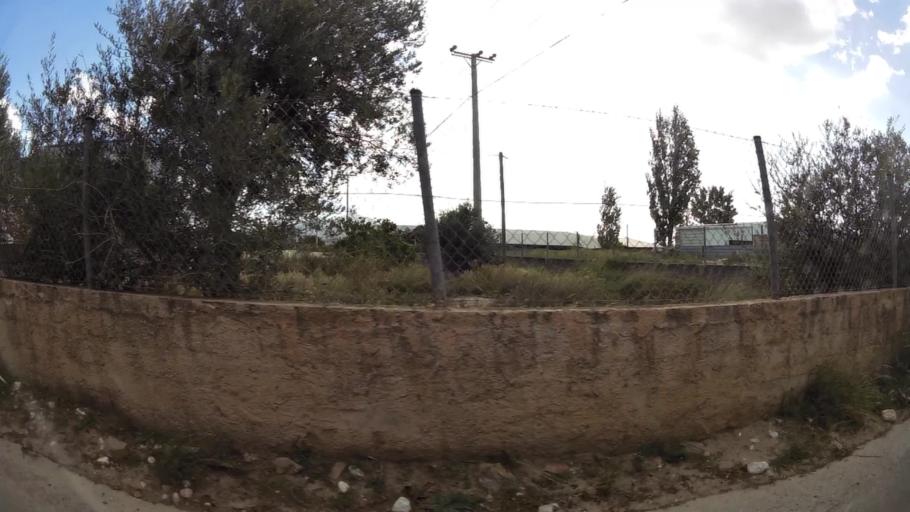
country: GR
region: Attica
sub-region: Nomarchia Anatolikis Attikis
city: Thrakomakedones
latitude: 38.1052
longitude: 23.7560
